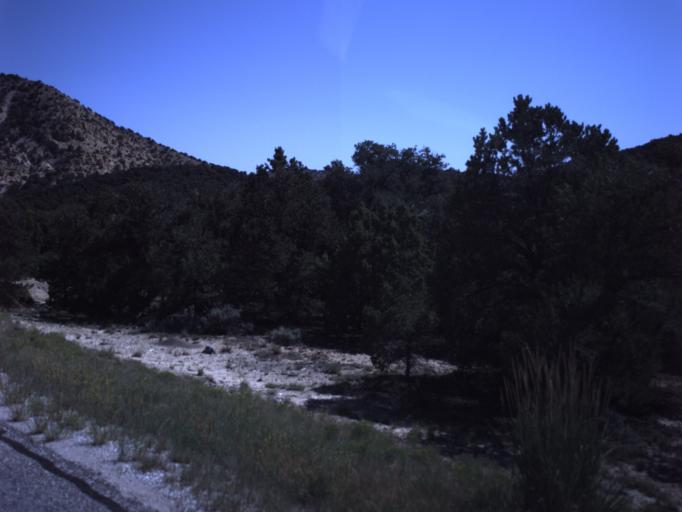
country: US
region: Utah
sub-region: Wayne County
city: Loa
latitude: 38.7353
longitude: -111.3941
